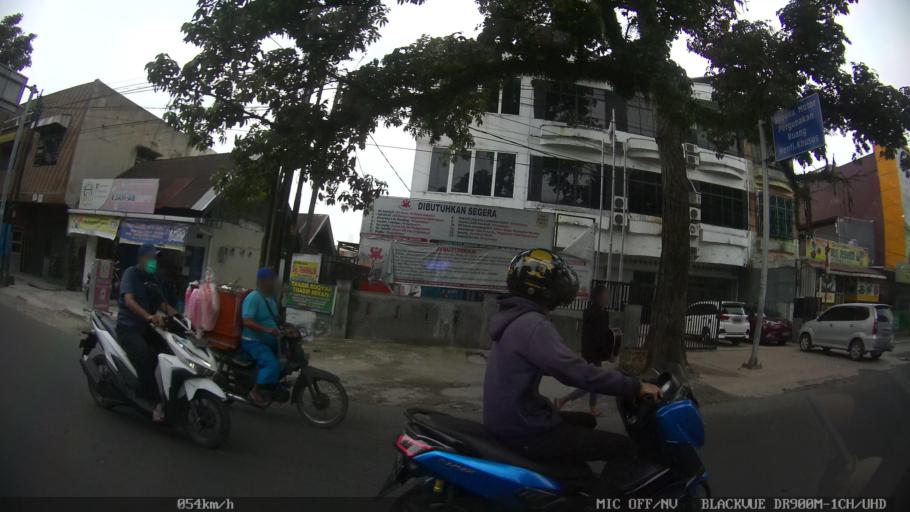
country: ID
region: North Sumatra
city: Medan
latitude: 3.5742
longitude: 98.6895
